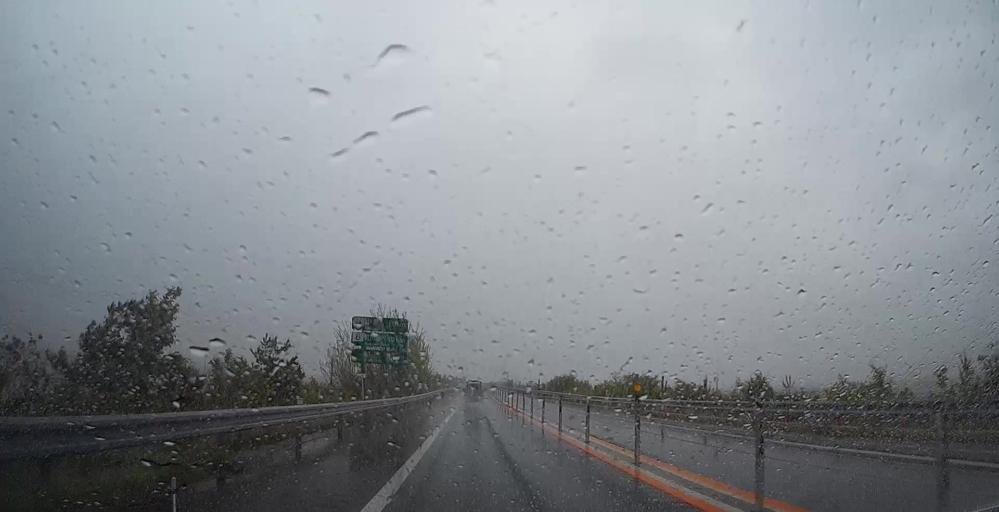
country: JP
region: Niigata
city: Shibata
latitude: 37.9709
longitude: 139.3017
